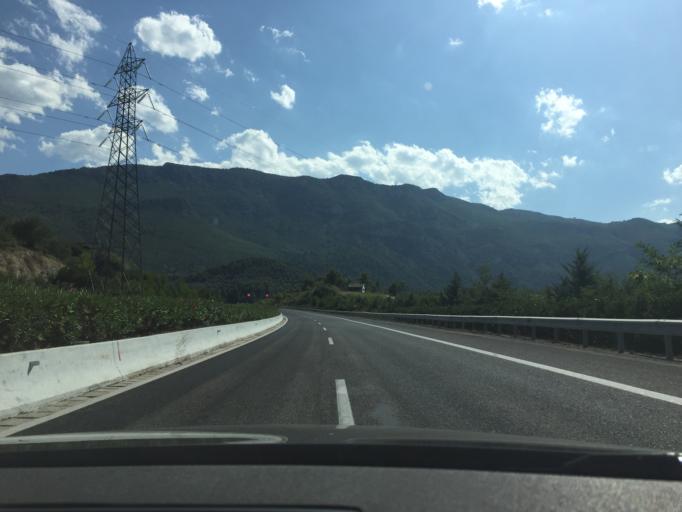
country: GR
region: Central Greece
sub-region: Nomos Fthiotidos
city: Ayios Konstandinos
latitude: 38.7537
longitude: 22.8808
